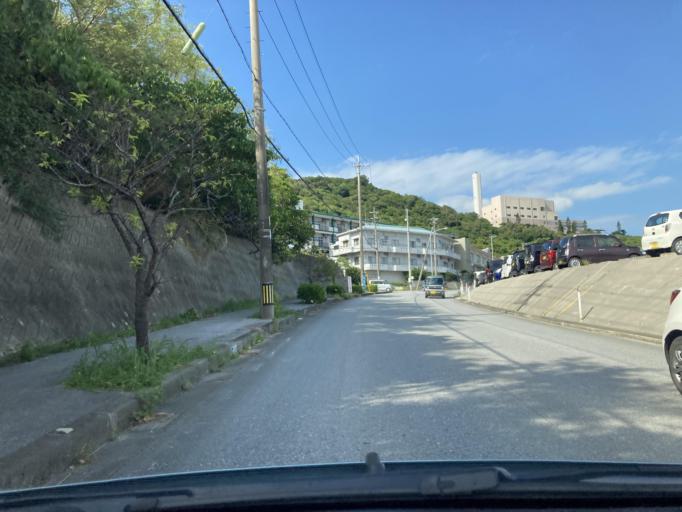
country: JP
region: Okinawa
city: Ginowan
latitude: 26.2758
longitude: 127.7967
